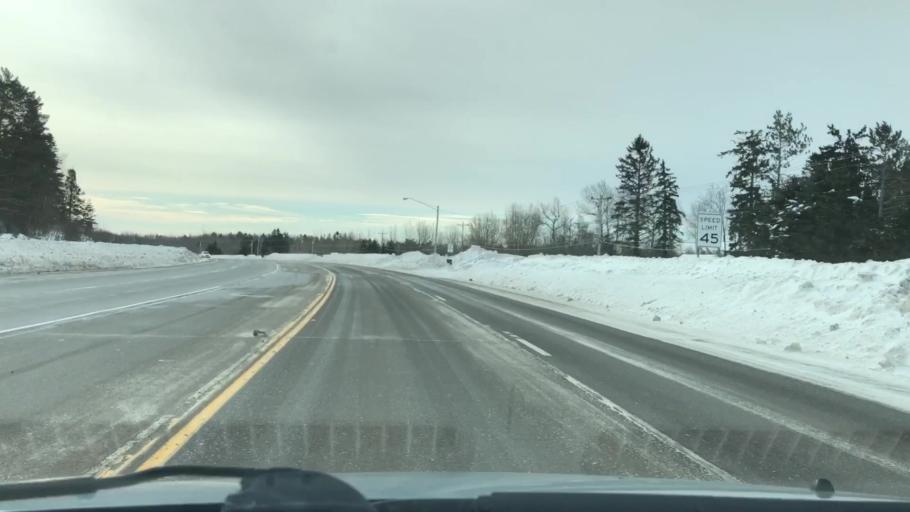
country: US
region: Minnesota
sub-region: Saint Louis County
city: Duluth
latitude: 46.7927
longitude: -92.1561
